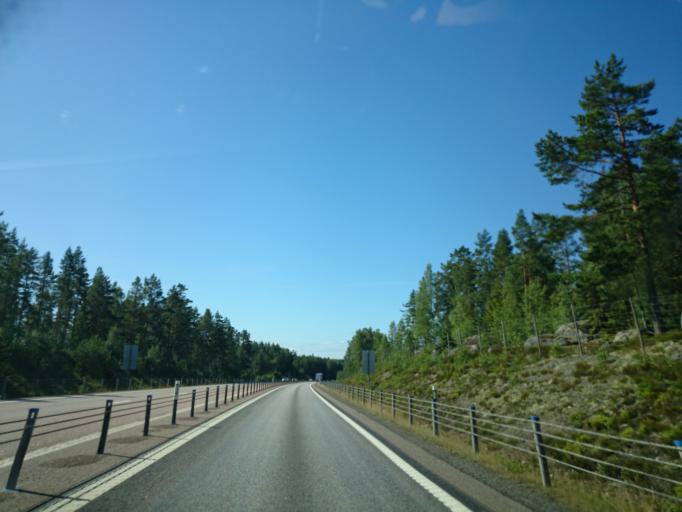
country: SE
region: Gaevleborg
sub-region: Soderhamns Kommun
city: Ljusne
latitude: 61.1455
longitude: 17.0323
